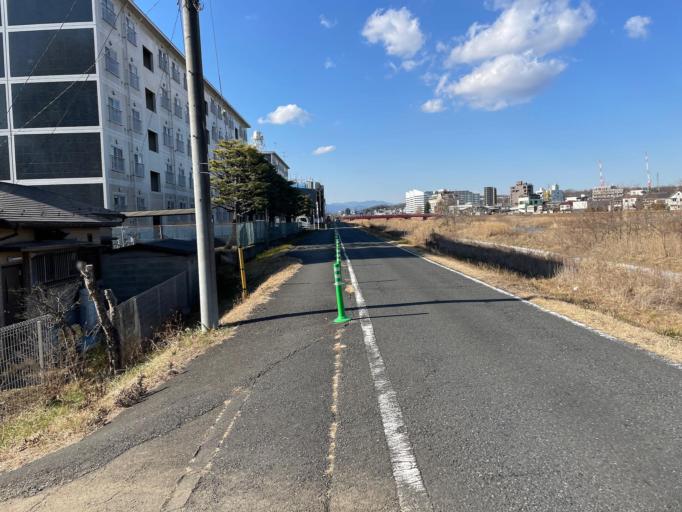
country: JP
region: Tokyo
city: Hachioji
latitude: 35.6583
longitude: 139.3518
